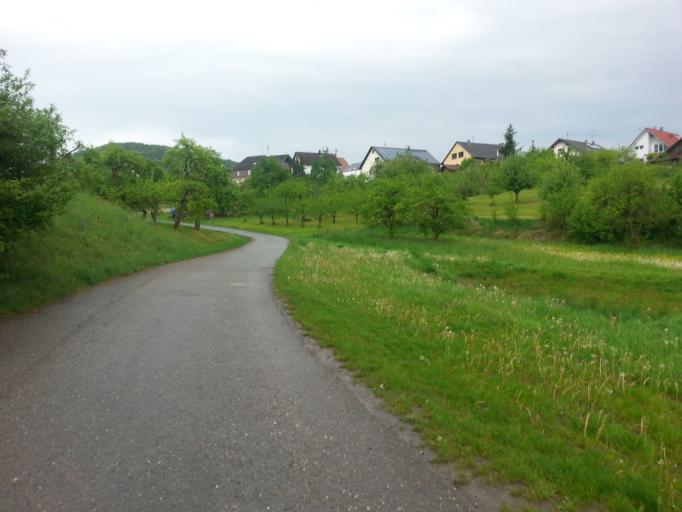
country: DE
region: Baden-Wuerttemberg
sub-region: Regierungsbezirk Stuttgart
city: Herrenberg
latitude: 48.5830
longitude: 8.9076
